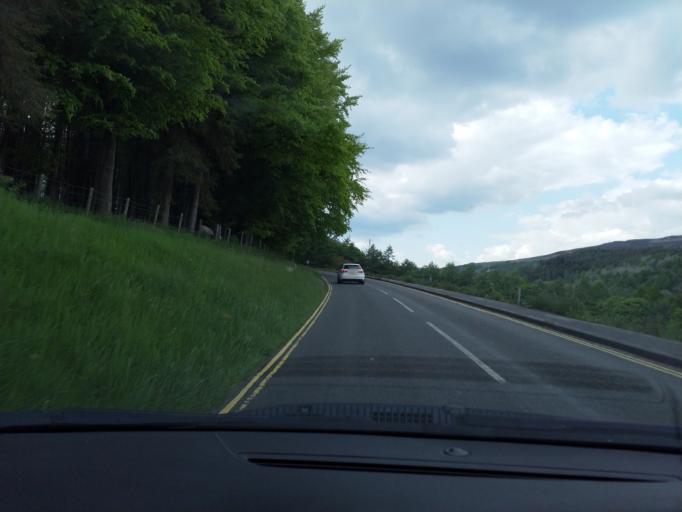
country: GB
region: England
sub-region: Derbyshire
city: Hope Valley
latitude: 53.3783
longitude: -1.7145
